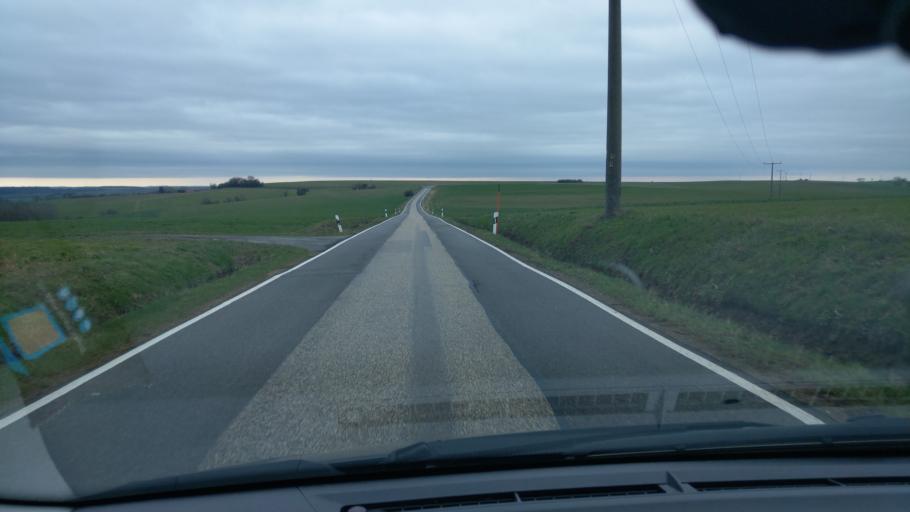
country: DE
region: Rheinland-Pfalz
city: Kleinbundenbach
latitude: 49.3234
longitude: 7.4351
